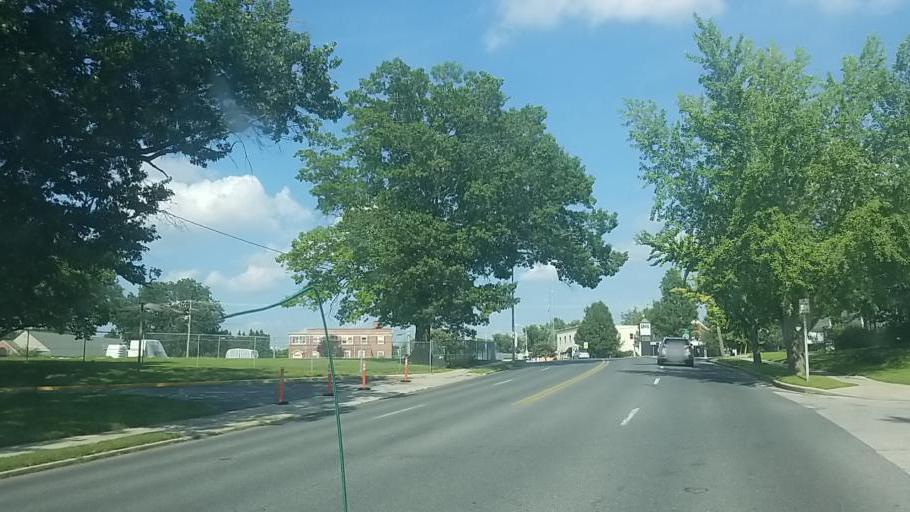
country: US
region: Maryland
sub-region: Wicomico County
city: Salisbury
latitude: 38.3653
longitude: -75.5883
